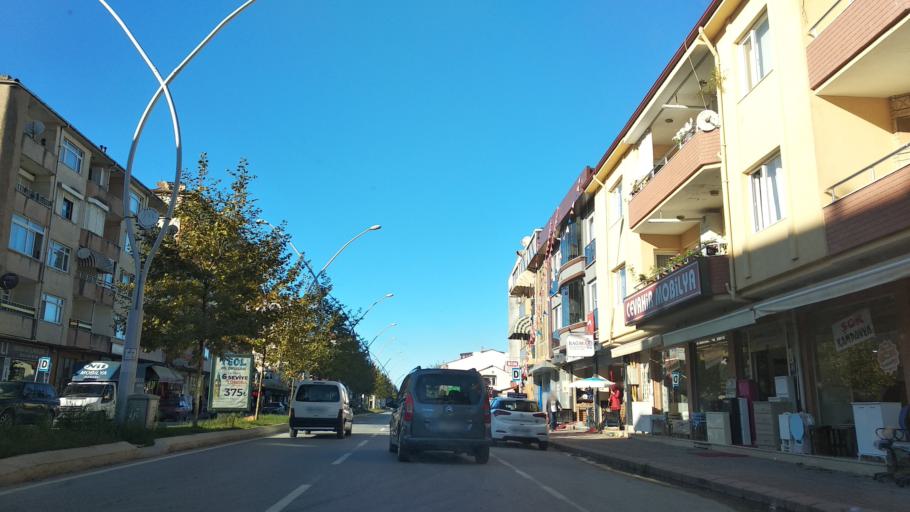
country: TR
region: Sakarya
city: Karasu
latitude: 41.1021
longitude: 30.6926
